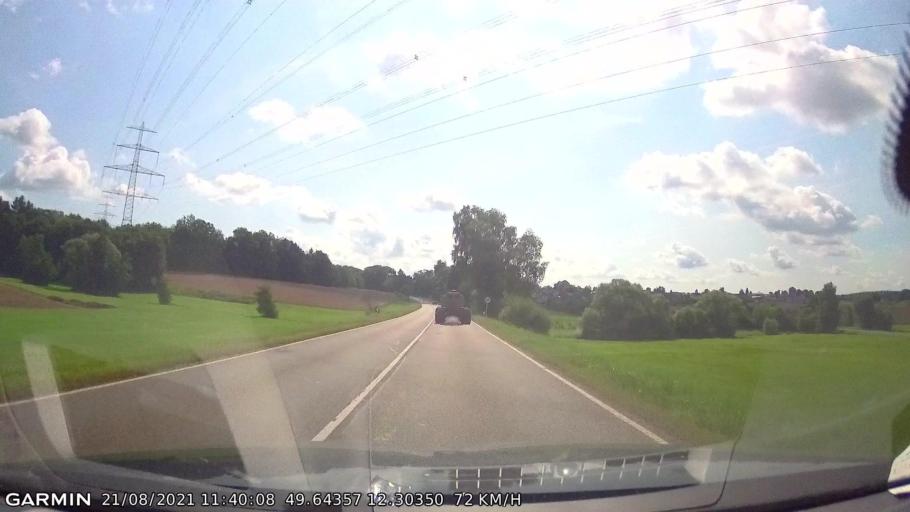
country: DE
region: Bavaria
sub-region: Upper Palatinate
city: Waldthurn
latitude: 49.6436
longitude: 12.3035
